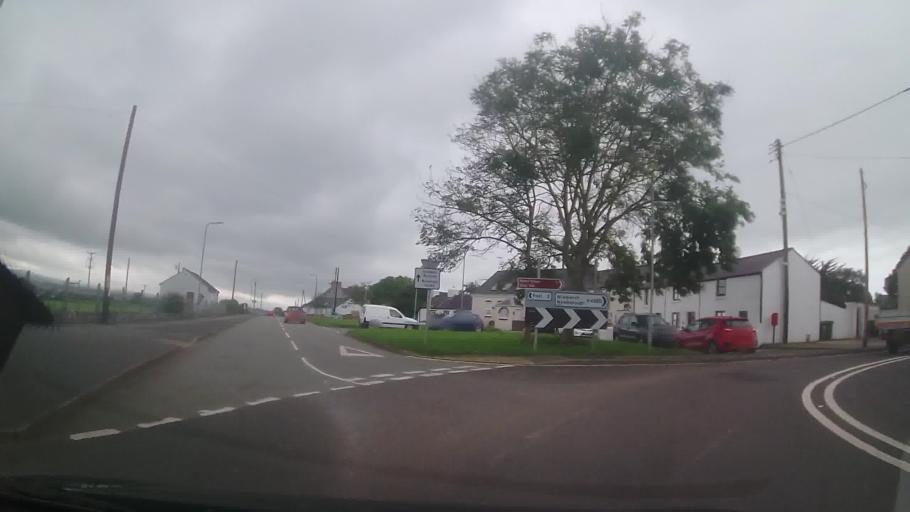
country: GB
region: Wales
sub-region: Gwynedd
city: Caernarfon
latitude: 53.1796
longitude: -4.2690
